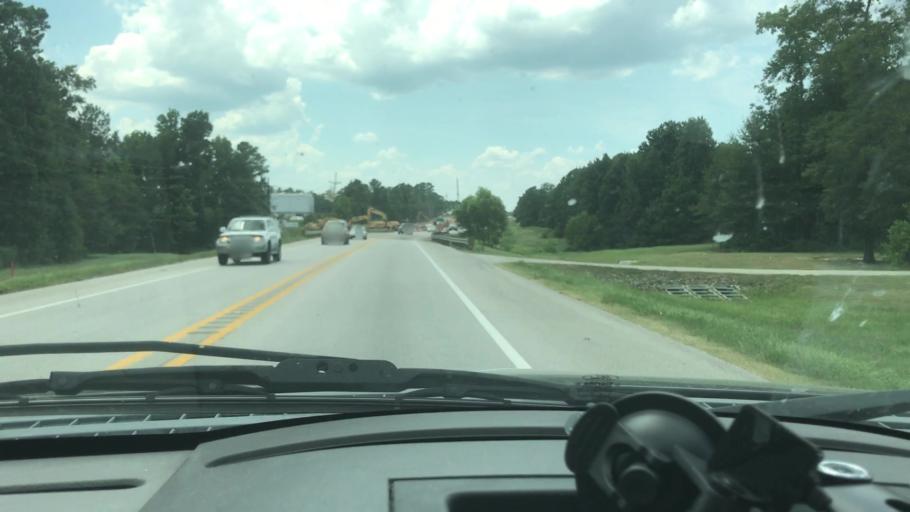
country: US
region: Texas
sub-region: Montgomery County
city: Conroe
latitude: 30.3498
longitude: -95.4523
